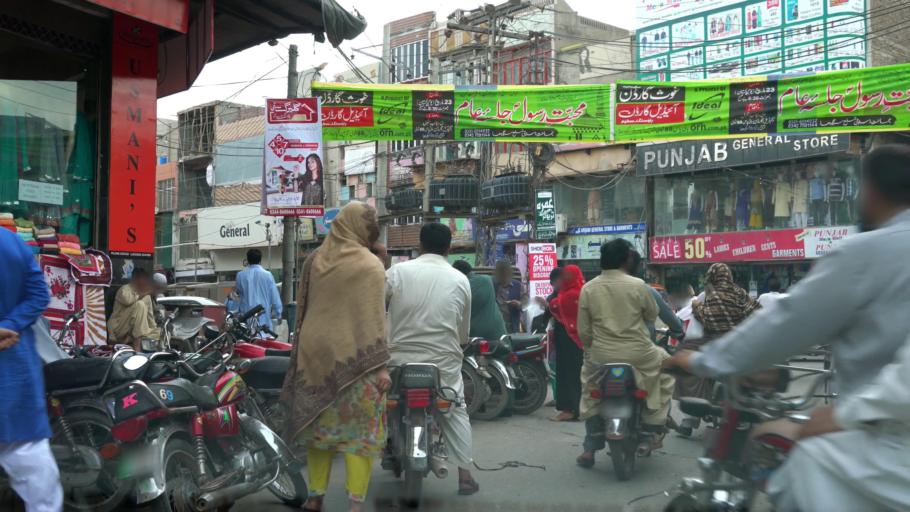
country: PK
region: Punjab
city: Sargodha
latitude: 32.0874
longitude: 72.6637
